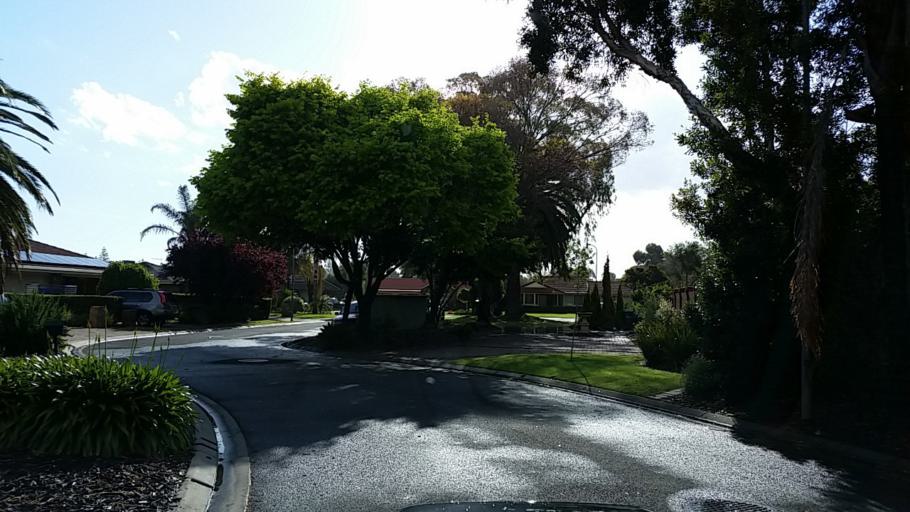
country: AU
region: South Australia
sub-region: Charles Sturt
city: Grange
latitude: -34.9037
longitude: 138.4994
